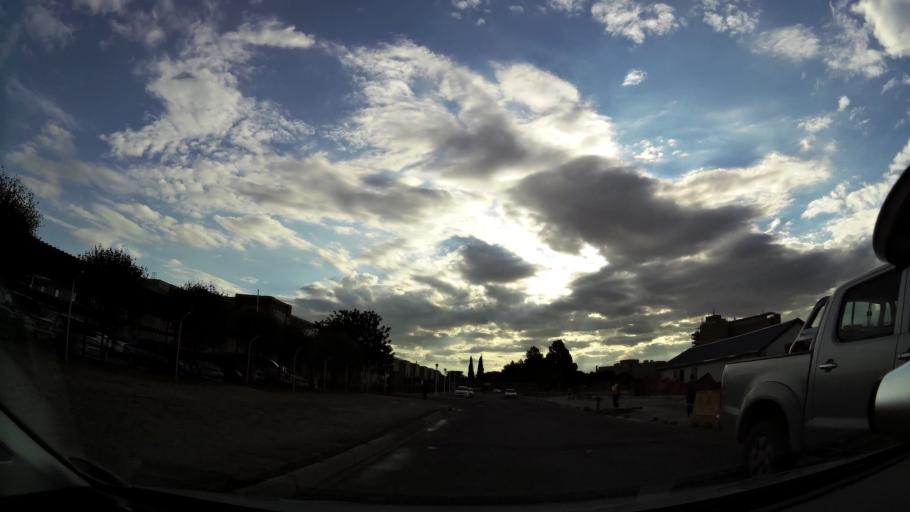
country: ZA
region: Orange Free State
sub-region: Lejweleputswa District Municipality
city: Welkom
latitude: -27.9874
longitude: 26.7317
